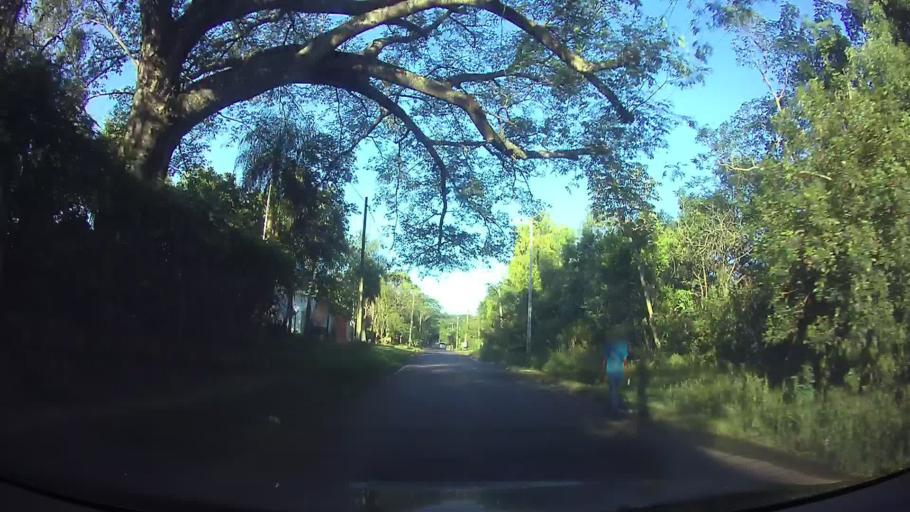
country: PY
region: Cordillera
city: San Bernardino
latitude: -25.3224
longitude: -57.2758
